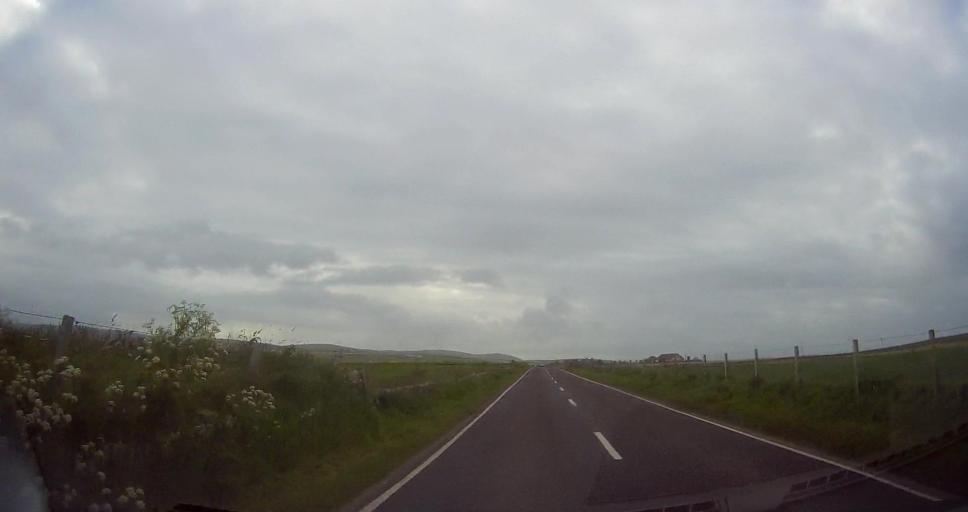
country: GB
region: Scotland
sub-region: Orkney Islands
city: Stromness
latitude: 58.9696
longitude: -3.2306
